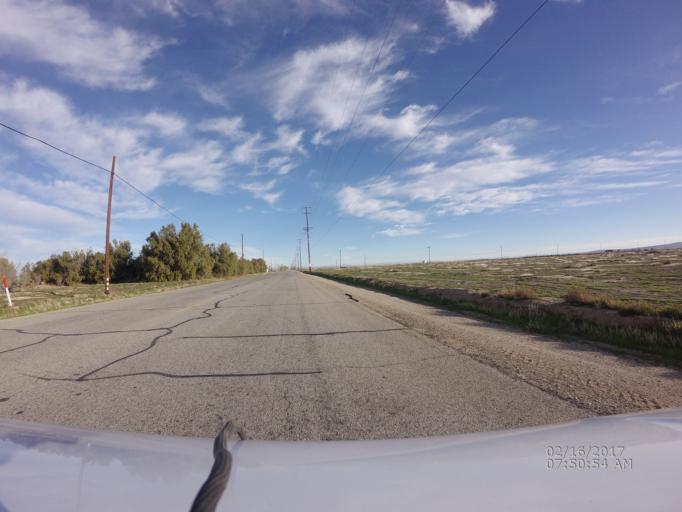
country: US
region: California
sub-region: Los Angeles County
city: Lancaster
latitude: 34.7181
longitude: -117.9697
